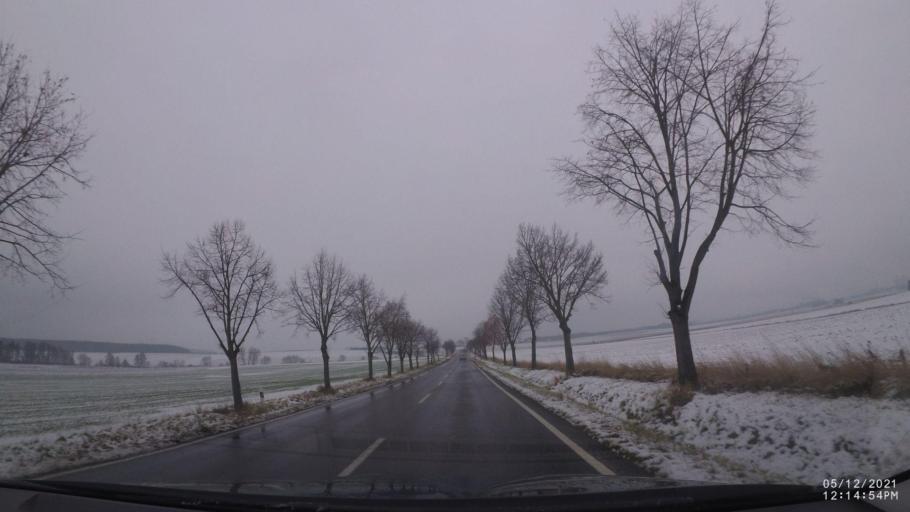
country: CZ
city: Ceske Mezirici
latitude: 50.3055
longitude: 16.0378
